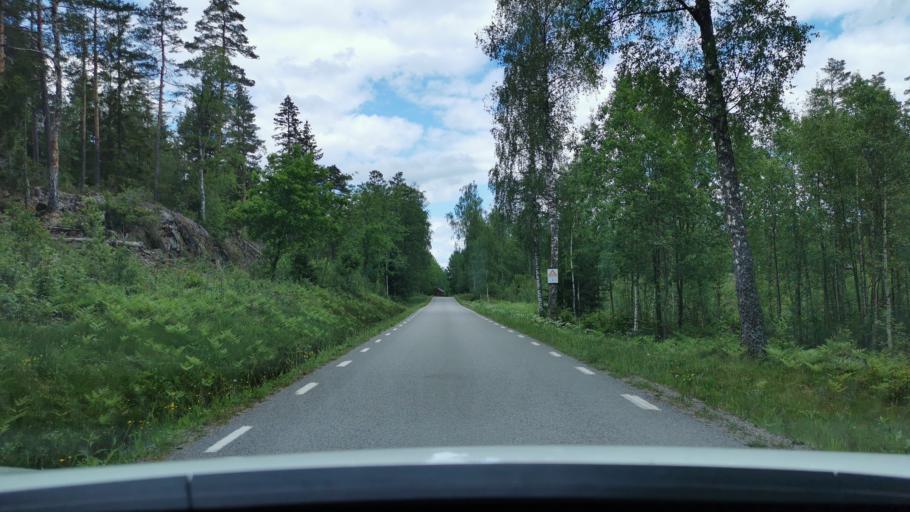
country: SE
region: Vaestra Goetaland
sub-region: Bengtsfors Kommun
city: Dals Langed
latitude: 58.8615
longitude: 12.3280
